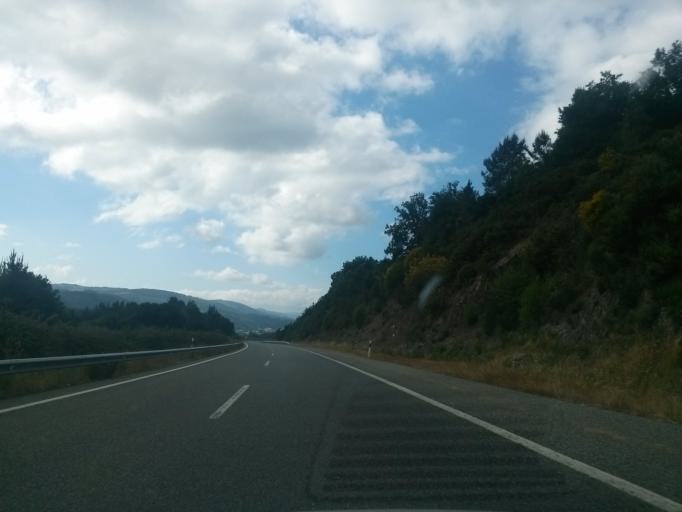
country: ES
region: Galicia
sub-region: Provincia de Lugo
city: Becerrea
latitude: 42.8999
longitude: -7.1880
